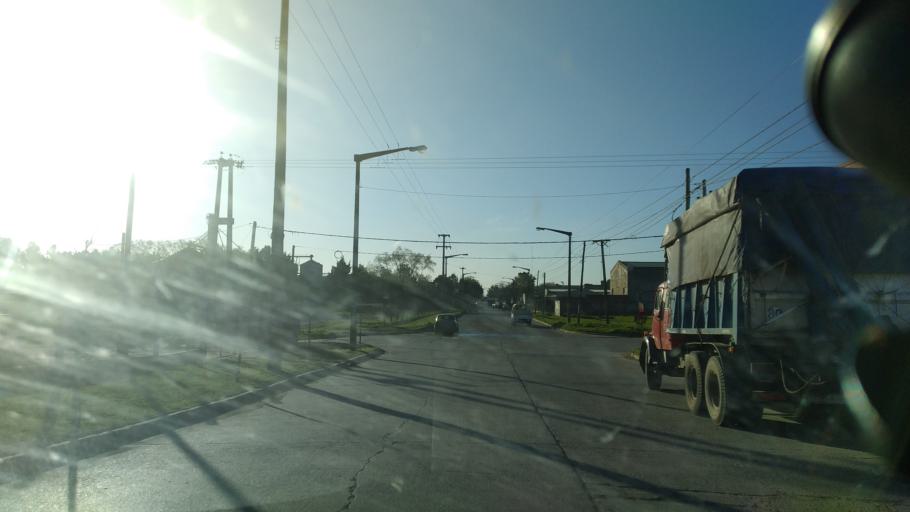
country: AR
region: Buenos Aires
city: Necochea
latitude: -38.5618
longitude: -58.7109
